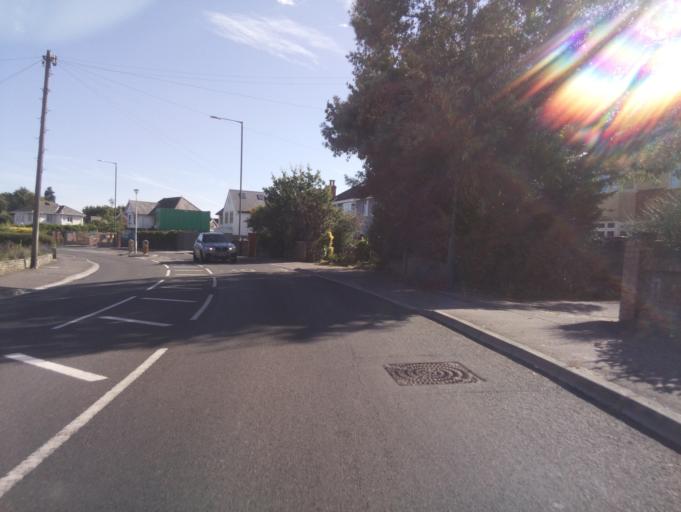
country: GB
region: England
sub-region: Dorset
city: Ferndown
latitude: 50.7727
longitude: -1.8880
